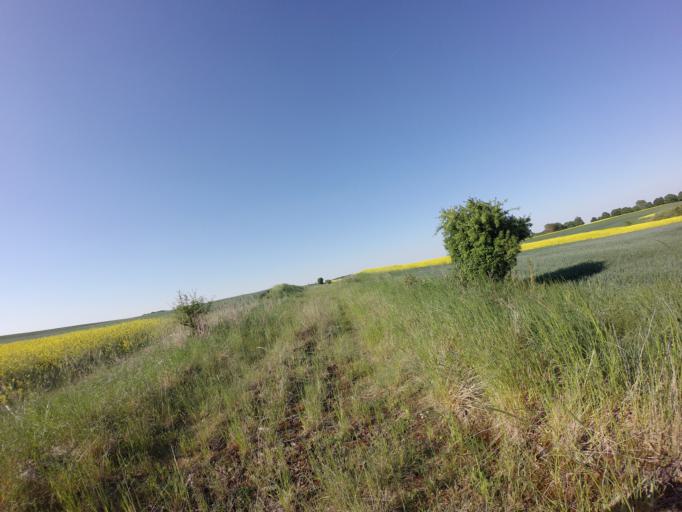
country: PL
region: West Pomeranian Voivodeship
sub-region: Powiat choszczenski
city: Choszczno
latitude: 53.1458
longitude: 15.3712
